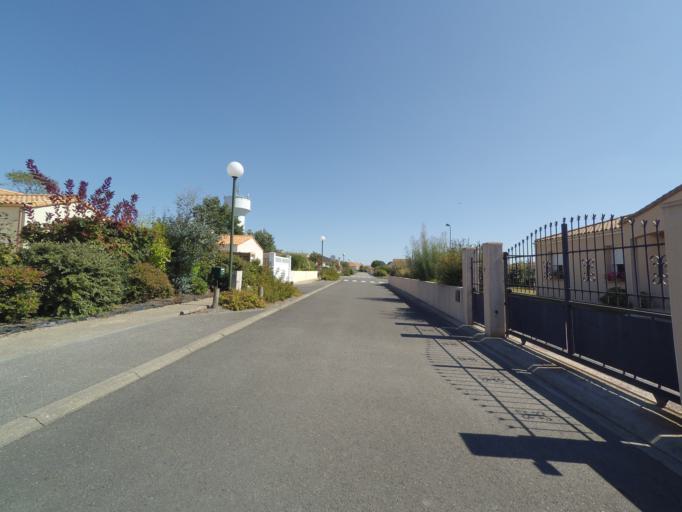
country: FR
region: Pays de la Loire
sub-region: Departement de la Loire-Atlantique
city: Vieillevigne
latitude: 46.9732
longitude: -1.4400
